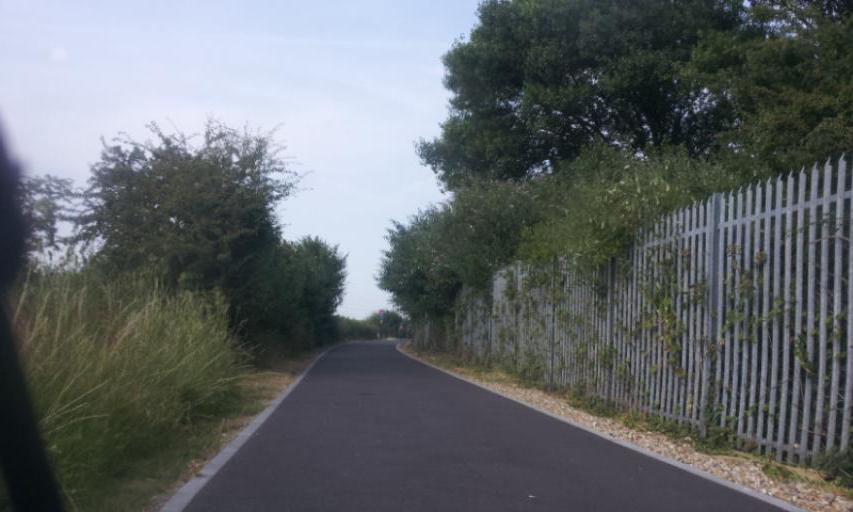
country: GB
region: England
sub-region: Greater London
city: Barking
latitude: 51.5083
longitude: 0.0917
